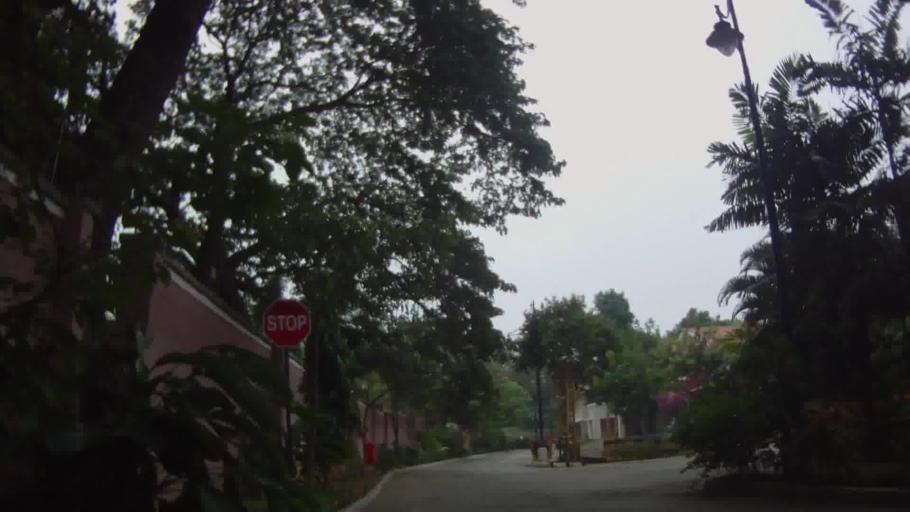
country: IN
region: Karnataka
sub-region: Bangalore Rural
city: Hoskote
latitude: 12.9596
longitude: 77.7489
